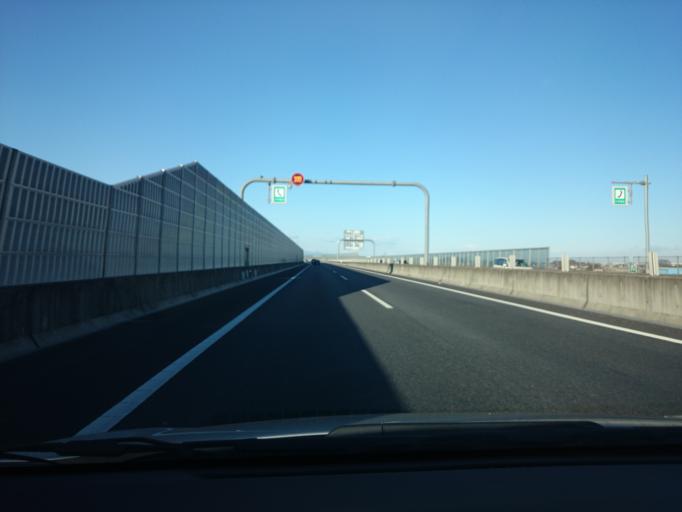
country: JP
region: Saitama
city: Kukichuo
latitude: 36.0510
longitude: 139.6408
